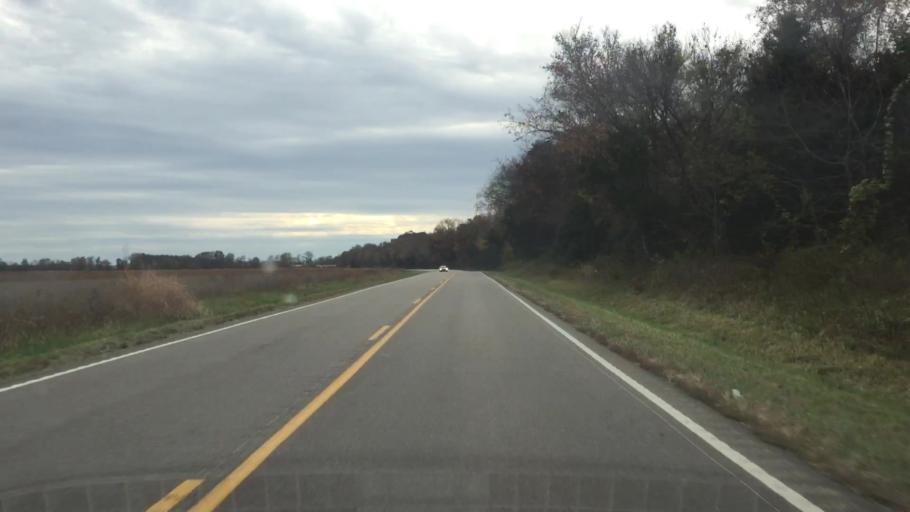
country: US
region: Missouri
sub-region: Callaway County
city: Holts Summit
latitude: 38.6167
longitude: -91.9668
